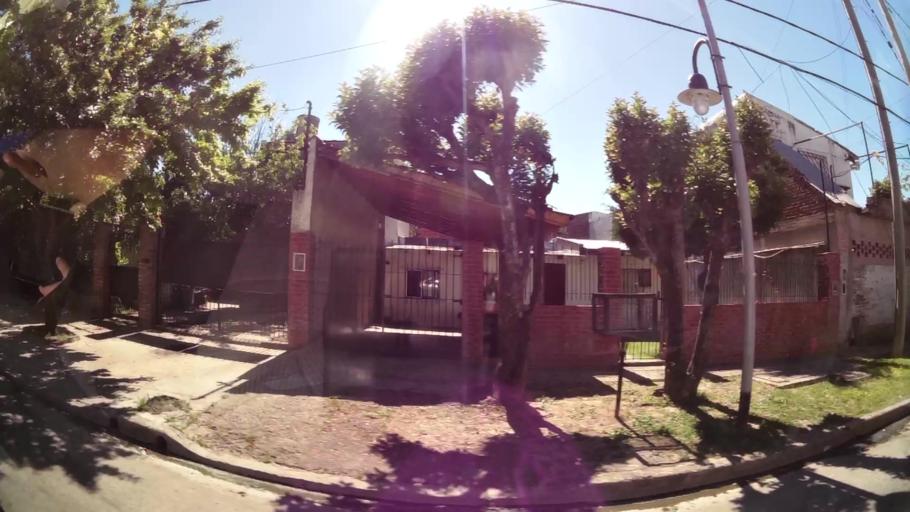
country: AR
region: Buenos Aires
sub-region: Partido de Tigre
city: Tigre
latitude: -34.5004
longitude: -58.6112
